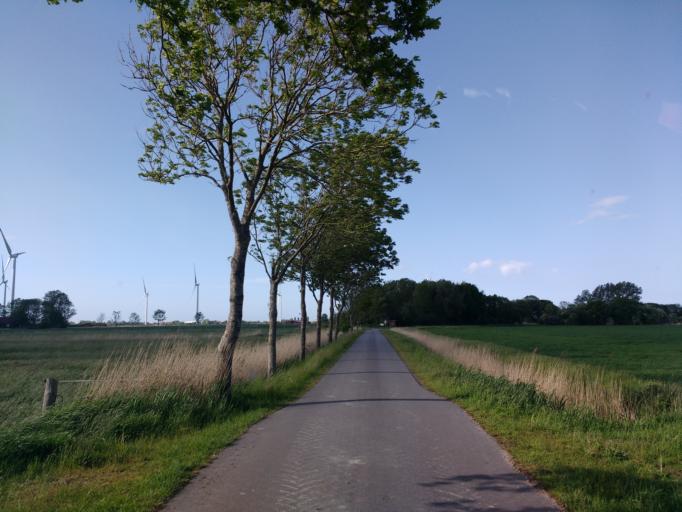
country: DE
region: Lower Saxony
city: Schillig
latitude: 53.6837
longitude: 7.9329
